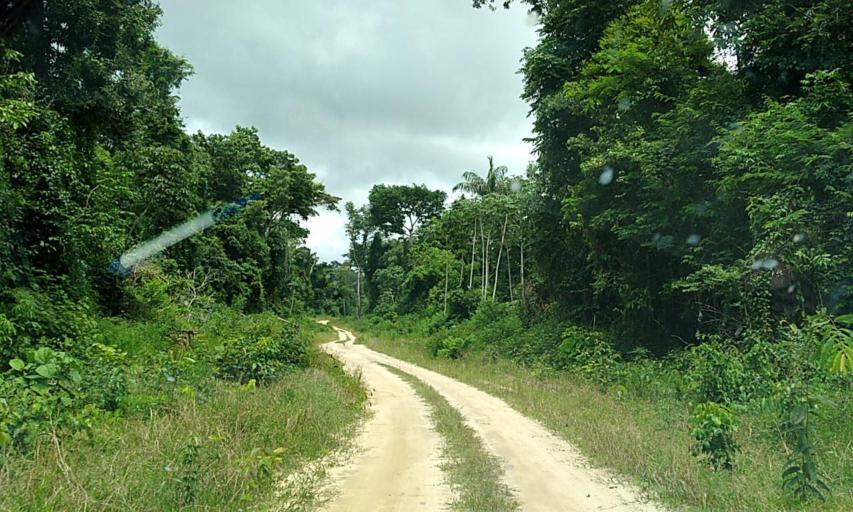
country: BR
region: Para
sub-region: Altamira
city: Altamira
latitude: -3.0648
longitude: -52.9086
